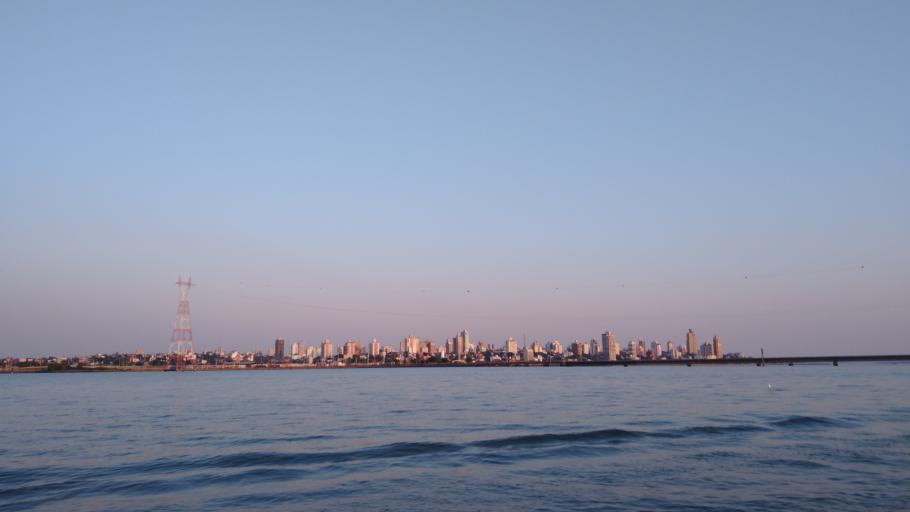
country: AR
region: Misiones
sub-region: Departamento de Capital
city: Posadas
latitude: -27.3798
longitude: -55.8746
